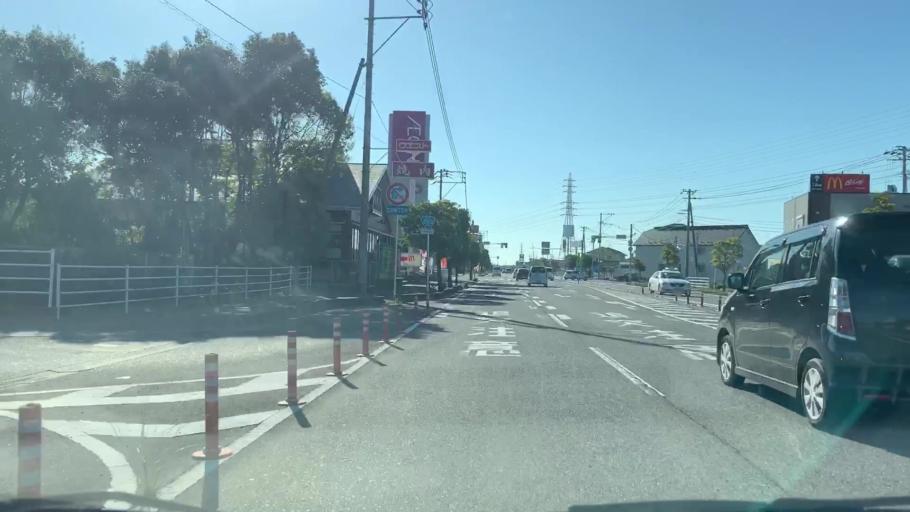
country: JP
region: Saga Prefecture
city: Saga-shi
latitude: 33.3039
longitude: 130.2789
